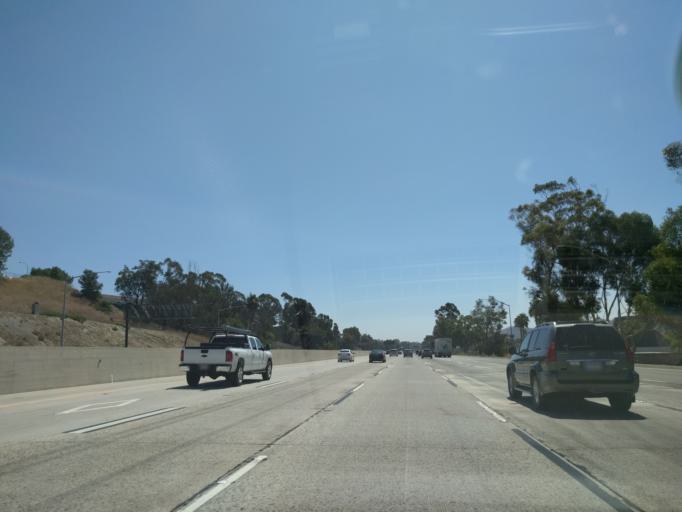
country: US
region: California
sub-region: Orange County
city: Ladera Ranch
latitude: 33.5563
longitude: -117.6731
